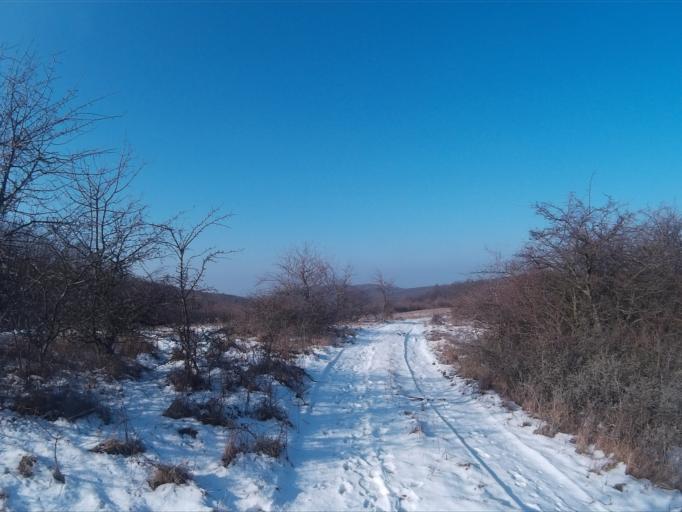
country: HU
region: Komarom-Esztergom
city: Labatlan
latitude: 47.7118
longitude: 18.4951
